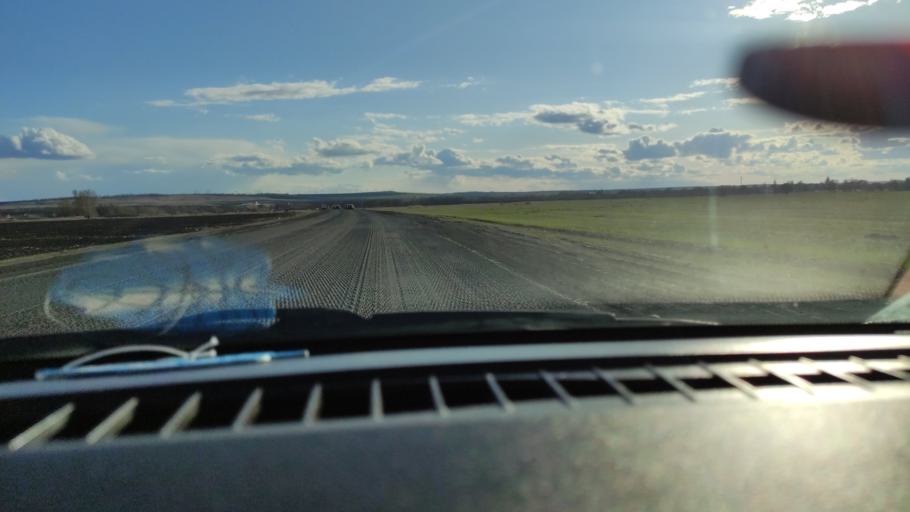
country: RU
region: Saratov
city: Yelshanka
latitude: 51.8084
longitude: 46.1976
